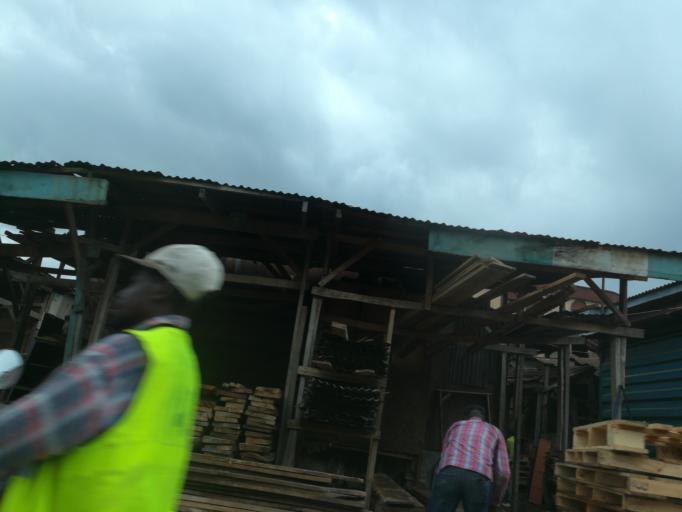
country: NG
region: Lagos
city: Oshodi
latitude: 6.5502
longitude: 3.3366
